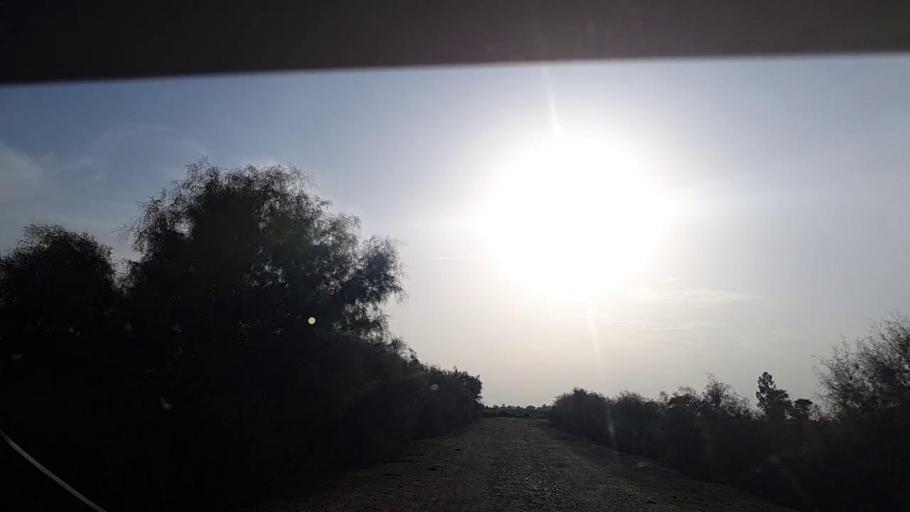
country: PK
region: Sindh
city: Khanpur
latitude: 27.8082
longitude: 69.3256
